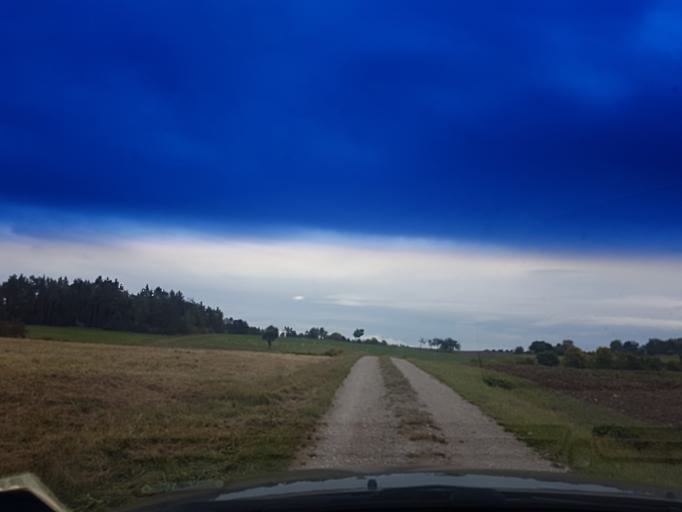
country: DE
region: Bavaria
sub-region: Upper Franconia
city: Poxdorf
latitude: 49.9006
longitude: 11.0962
